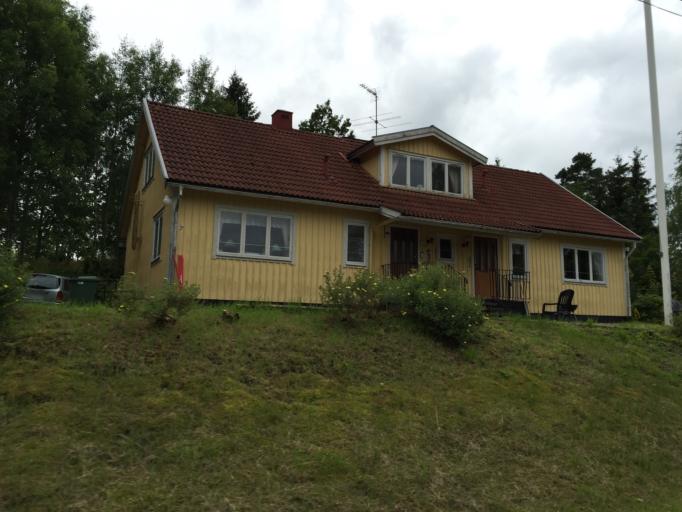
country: SE
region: Stockholm
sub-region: Salems Kommun
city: Ronninge
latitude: 59.2615
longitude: 17.7166
